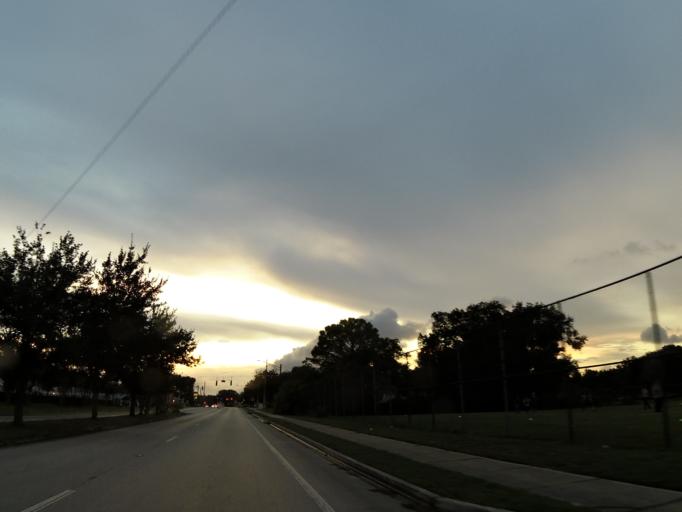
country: US
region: Florida
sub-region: Duval County
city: Jacksonville
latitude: 30.3665
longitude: -81.5926
